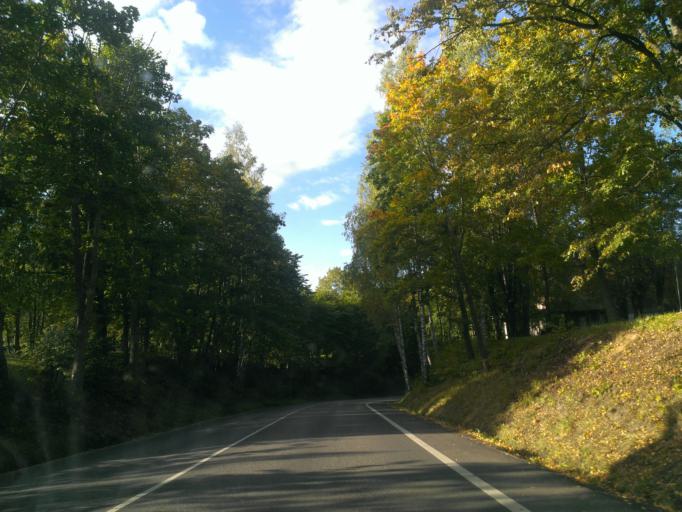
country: LV
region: Sigulda
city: Sigulda
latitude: 57.1619
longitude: 24.8509
